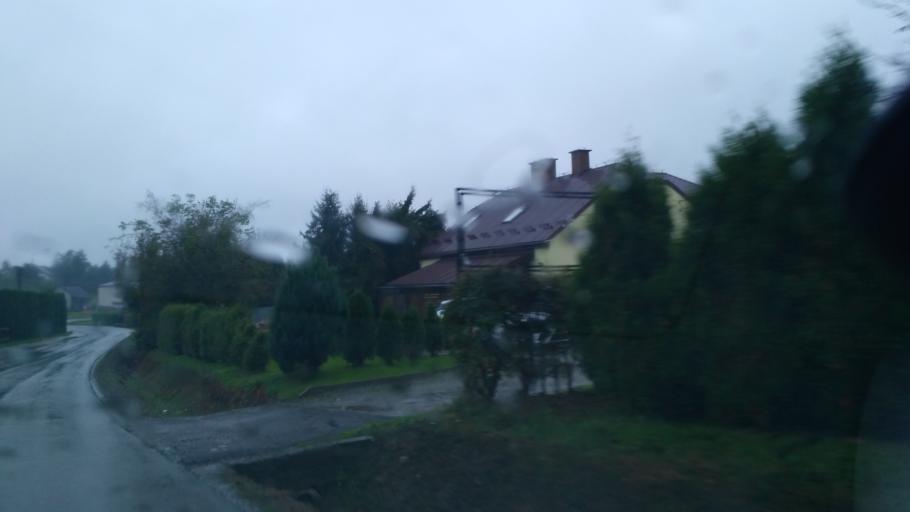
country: PL
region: Subcarpathian Voivodeship
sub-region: Powiat krosnienski
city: Korczyna
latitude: 49.7035
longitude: 21.8124
